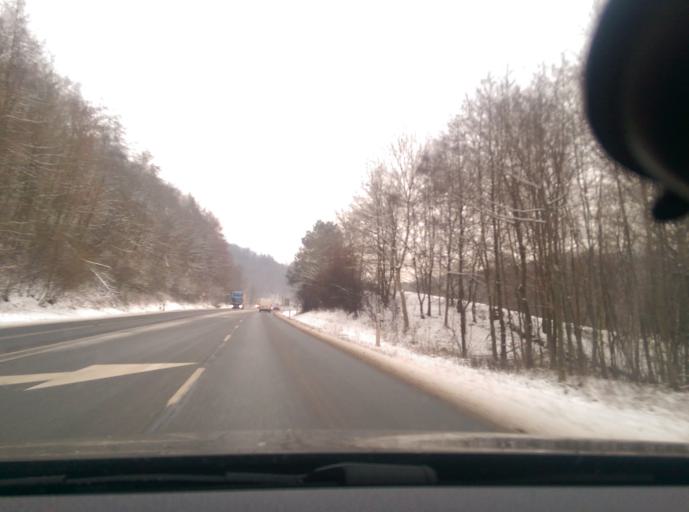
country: DE
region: Hesse
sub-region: Regierungsbezirk Kassel
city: Helsa
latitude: 51.2662
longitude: 9.6714
